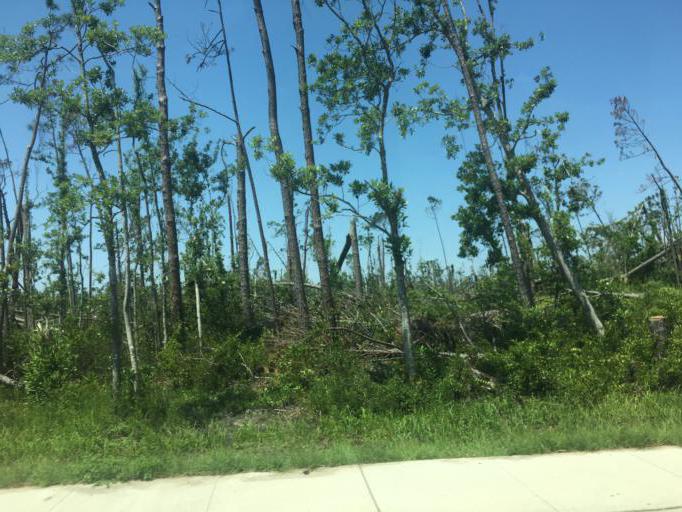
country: US
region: Florida
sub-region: Bay County
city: Hiland Park
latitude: 30.2120
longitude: -85.6281
